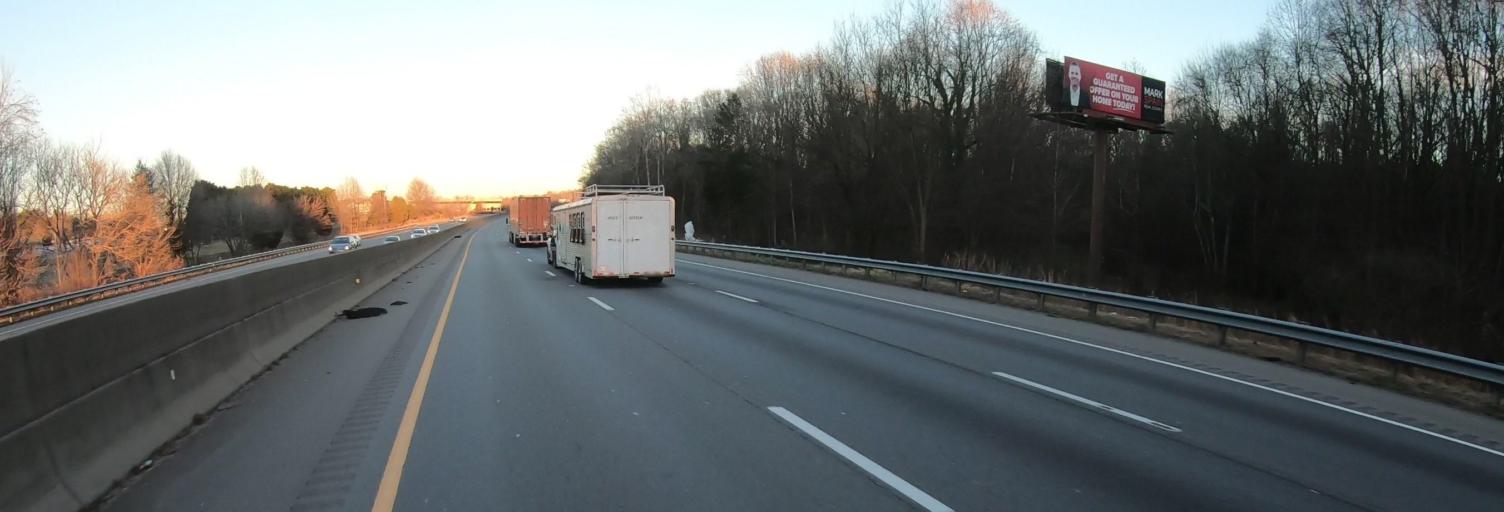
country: US
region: North Carolina
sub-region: Gaston County
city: Gastonia
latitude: 35.2840
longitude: -81.2060
